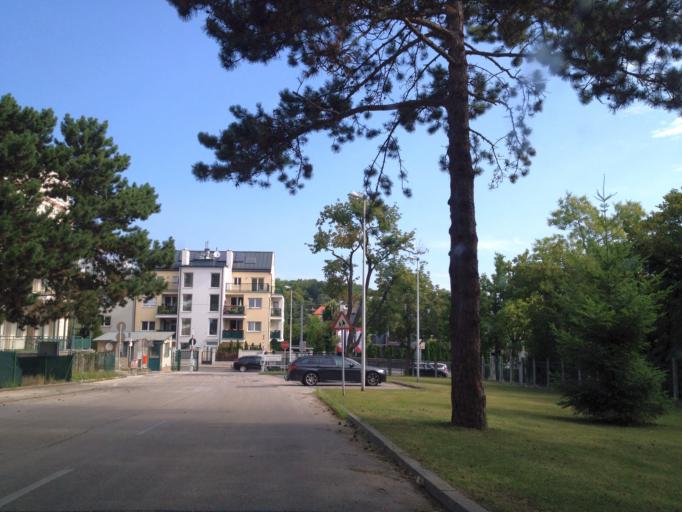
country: AT
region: Lower Austria
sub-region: Politischer Bezirk Modling
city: Perchtoldsdorf
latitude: 48.1769
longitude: 16.2725
